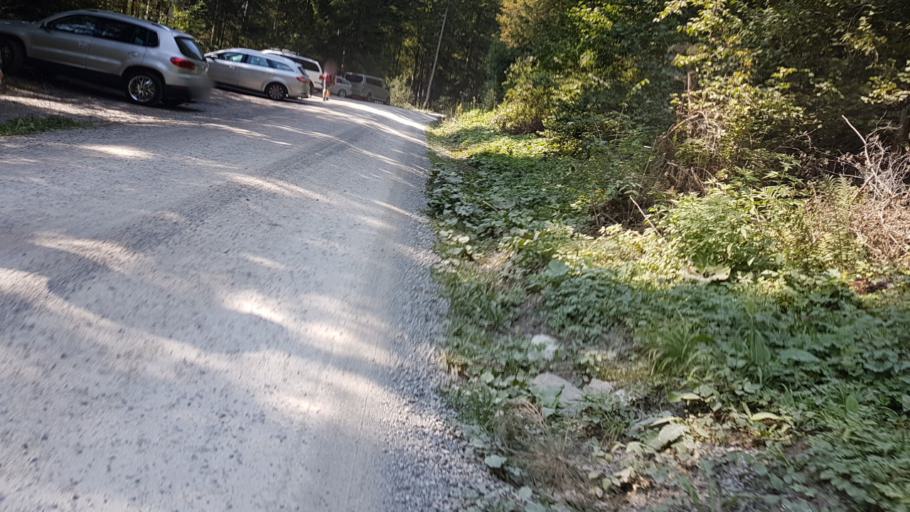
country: CH
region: Bern
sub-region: Frutigen-Niedersimmental District
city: Aeschi
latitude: 46.6304
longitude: 7.7461
